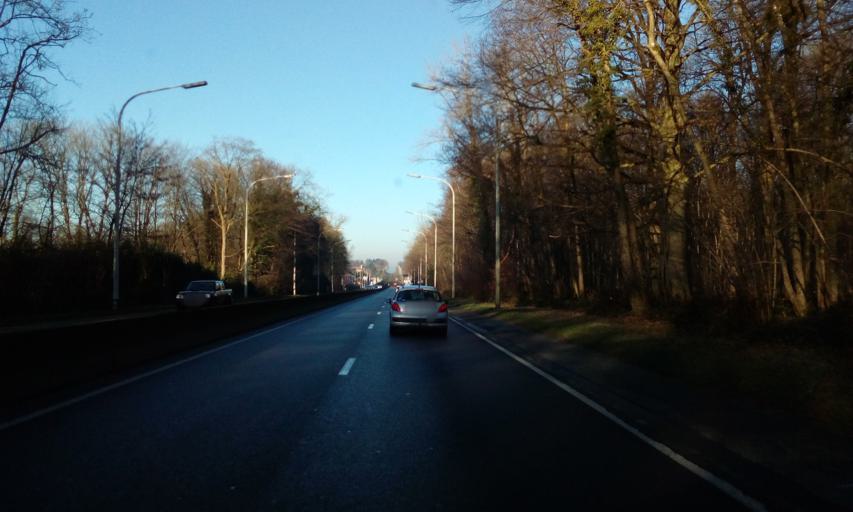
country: BE
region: Wallonia
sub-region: Province du Hainaut
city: Gerpinnes
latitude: 50.3570
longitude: 4.4707
